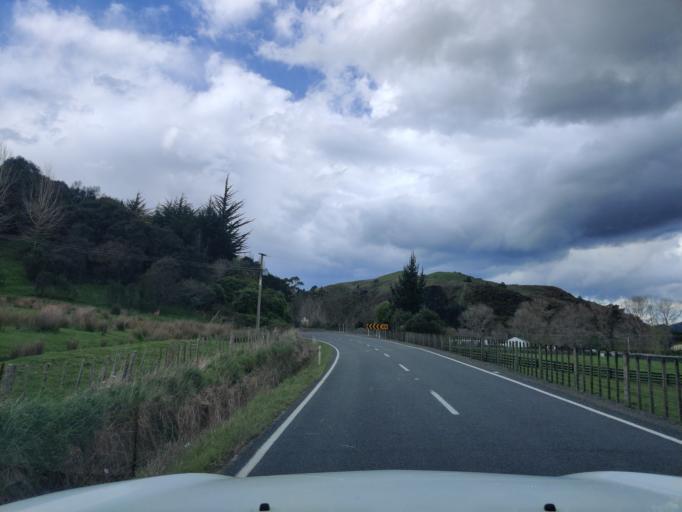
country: NZ
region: Manawatu-Wanganui
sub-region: Wanganui District
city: Wanganui
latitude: -39.8438
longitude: 175.1527
